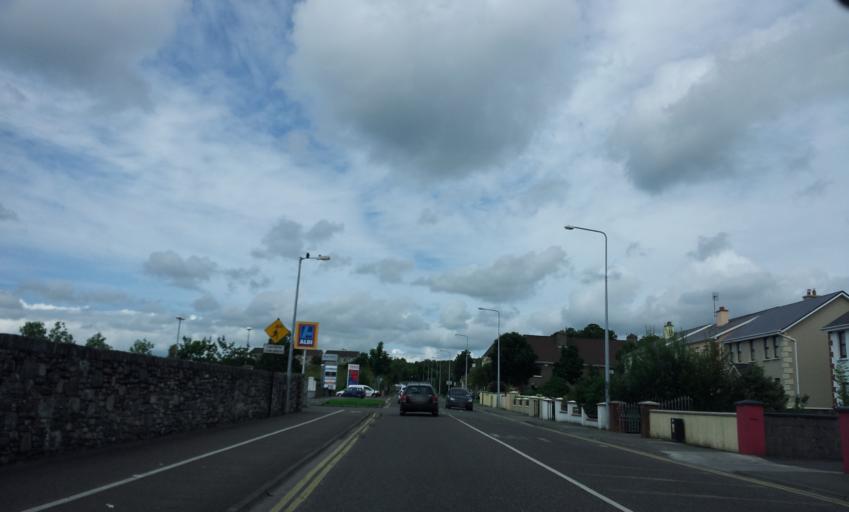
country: IE
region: Munster
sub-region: Ciarrai
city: Cill Airne
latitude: 52.0612
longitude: -9.4931
